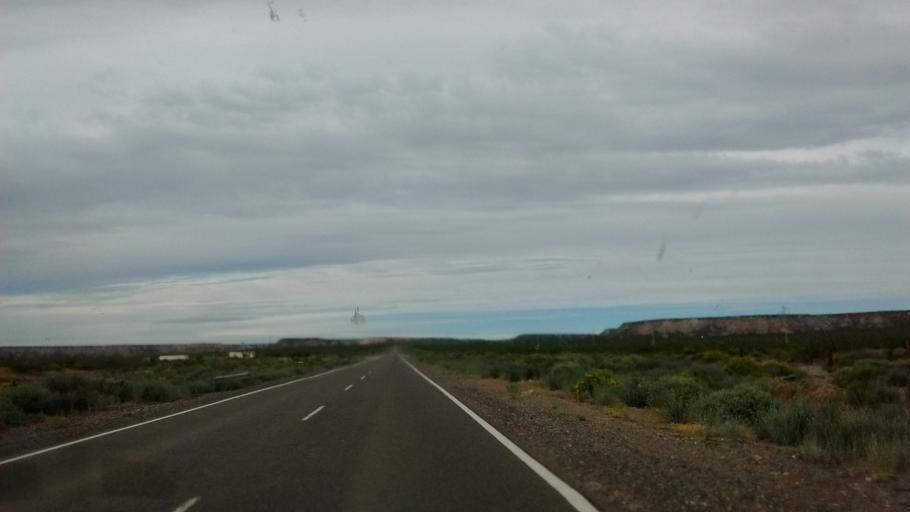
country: AR
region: Rio Negro
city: Catriel
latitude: -38.1761
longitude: -67.9548
